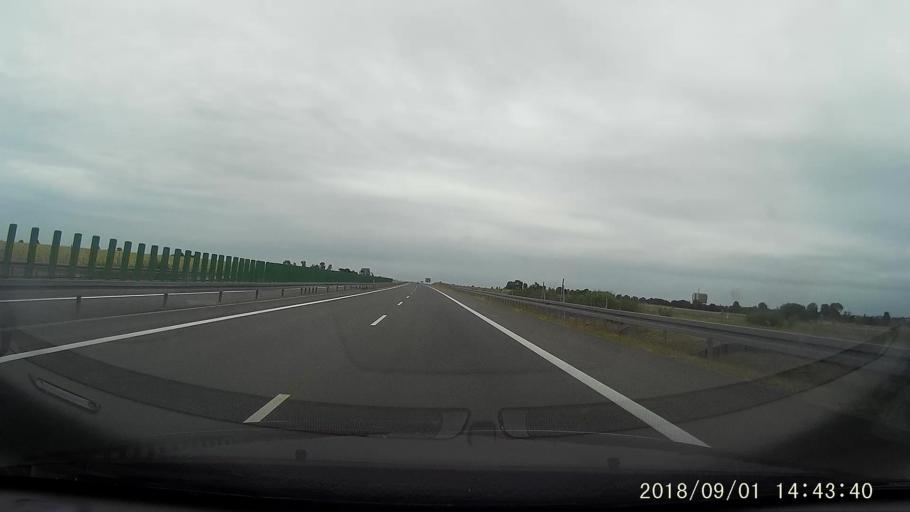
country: PL
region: Lubusz
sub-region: Powiat gorzowski
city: Jenin
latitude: 52.7552
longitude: 15.1454
